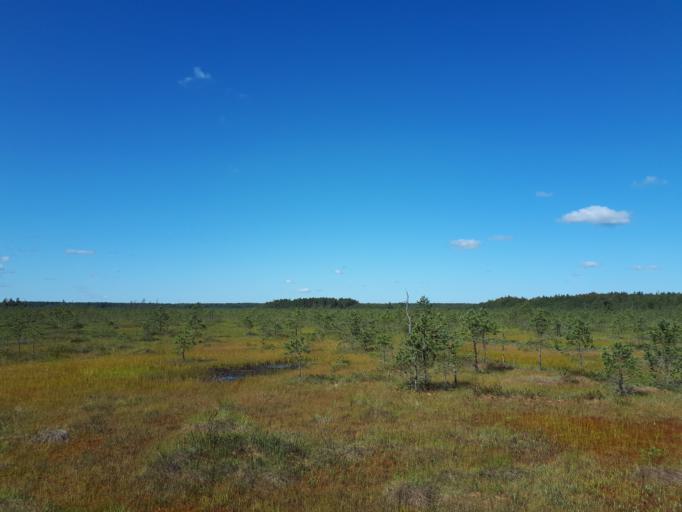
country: BY
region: Vitebsk
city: Rasony
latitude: 56.0586
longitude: 28.6278
